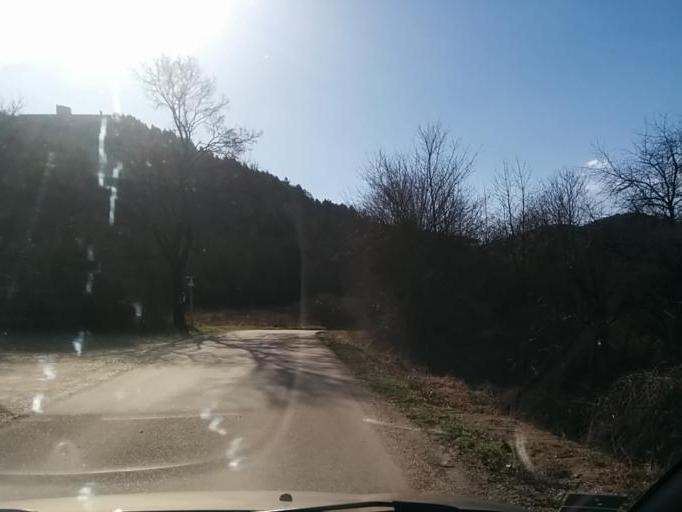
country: SK
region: Nitriansky
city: Cachtice
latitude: 48.7298
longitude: 17.7587
